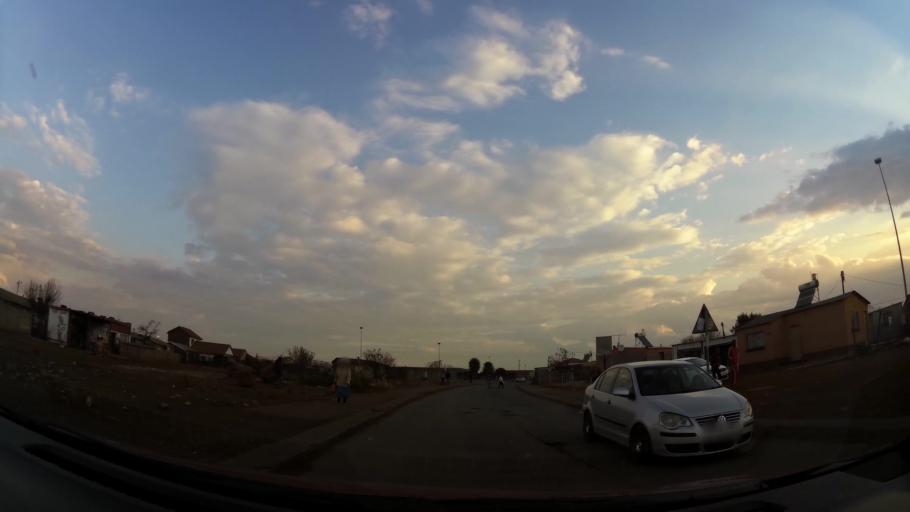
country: ZA
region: Gauteng
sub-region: City of Johannesburg Metropolitan Municipality
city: Orange Farm
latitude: -26.5614
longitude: 27.8377
